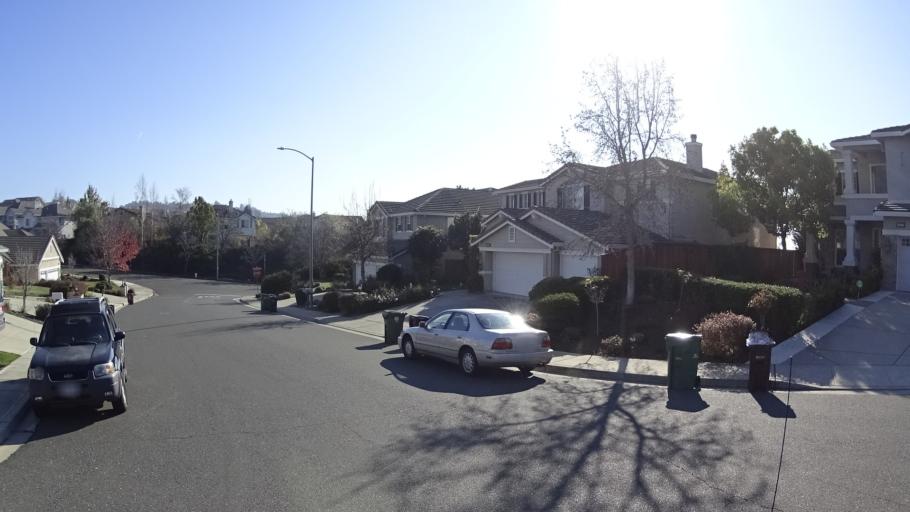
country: US
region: California
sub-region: Alameda County
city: Fairview
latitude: 37.6920
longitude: -122.0388
